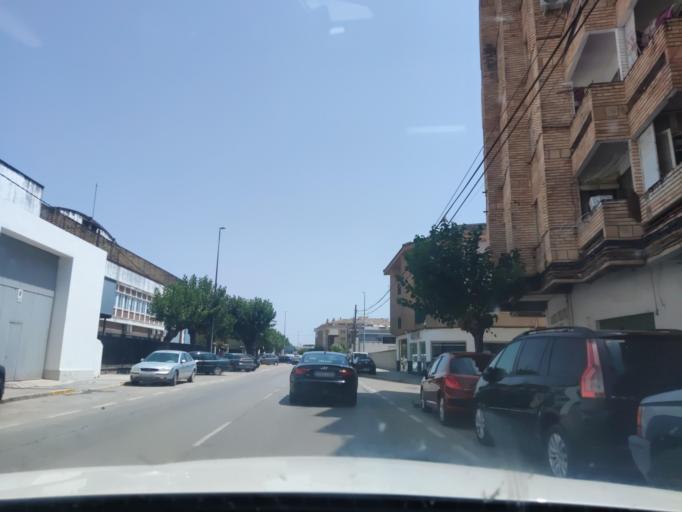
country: ES
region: Castille-La Mancha
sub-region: Provincia de Albacete
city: Hellin
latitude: 38.5080
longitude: -1.6896
